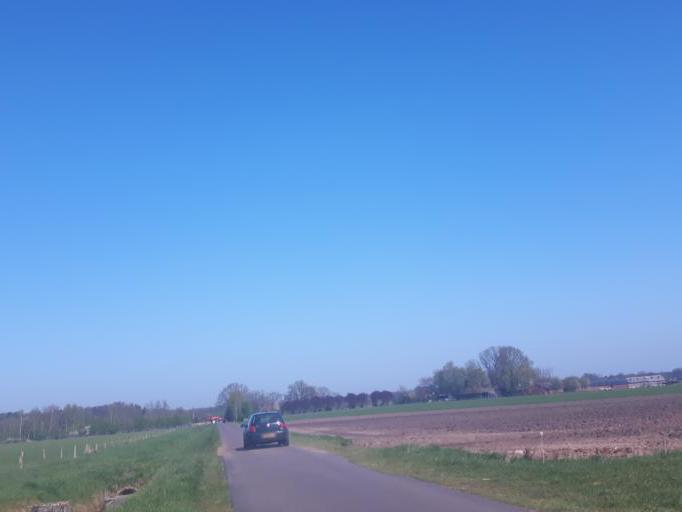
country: NL
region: Overijssel
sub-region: Gemeente Haaksbergen
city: Haaksbergen
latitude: 52.1325
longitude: 6.7988
